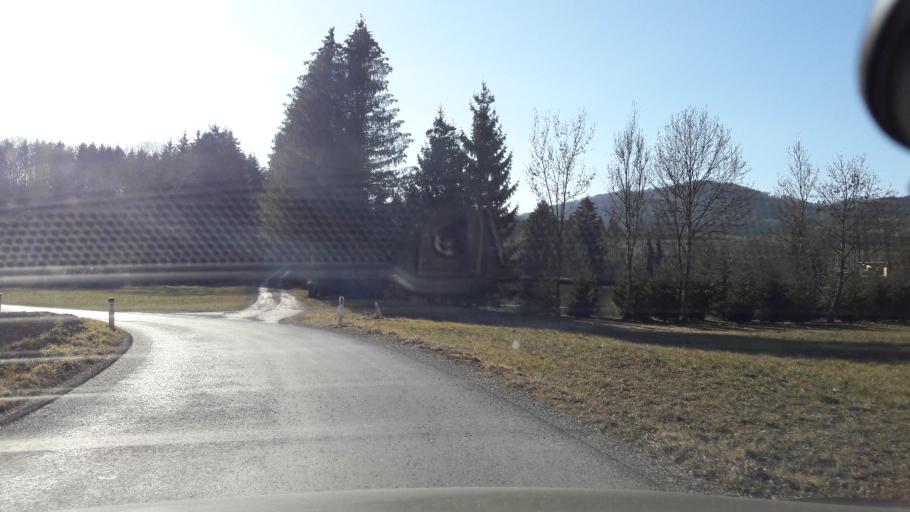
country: AT
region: Styria
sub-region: Politischer Bezirk Graz-Umgebung
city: Eisbach
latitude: 47.1130
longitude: 15.2746
